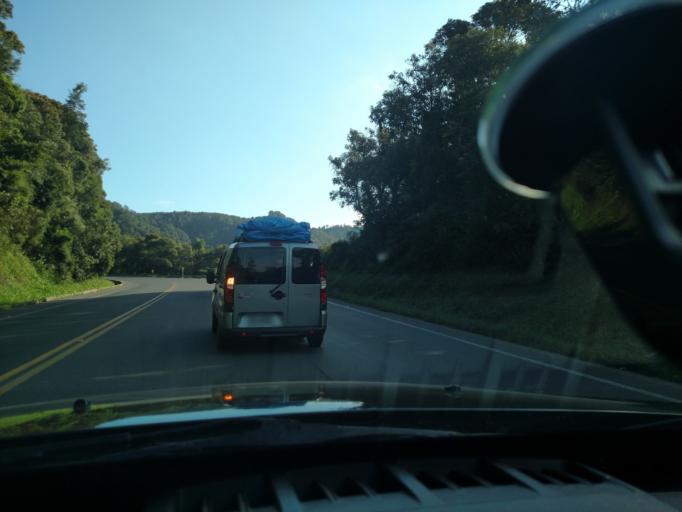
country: BR
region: Santa Catarina
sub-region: Otacilio Costa
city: Otacilio Costa
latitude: -27.2923
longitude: -50.0784
